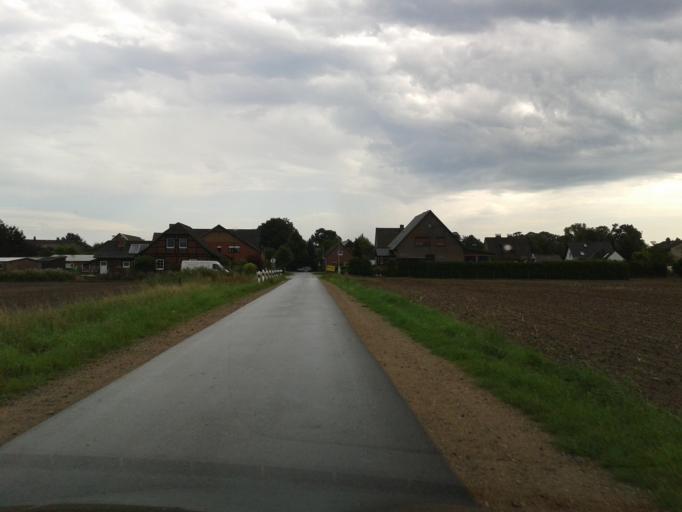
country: DE
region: Lower Saxony
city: Woltersdorf
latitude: 52.9522
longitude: 11.2068
